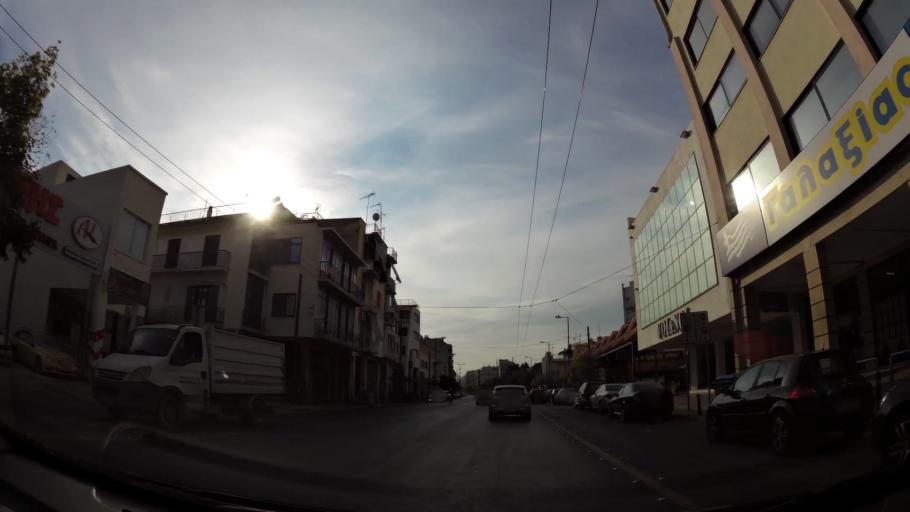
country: GR
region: Attica
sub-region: Nomarchia Athinas
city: Athens
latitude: 37.9938
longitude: 23.7132
